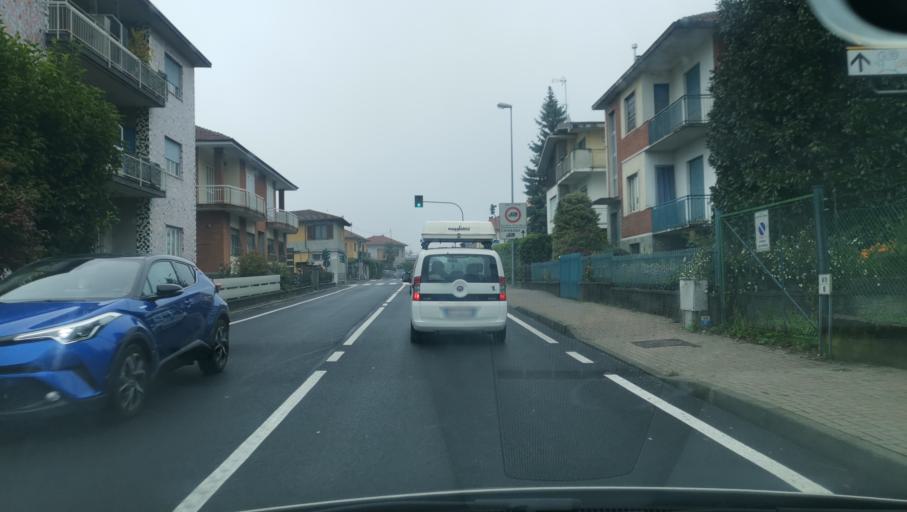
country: IT
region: Piedmont
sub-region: Provincia di Torino
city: Castiglione Torinese
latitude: 45.1209
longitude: 7.8123
